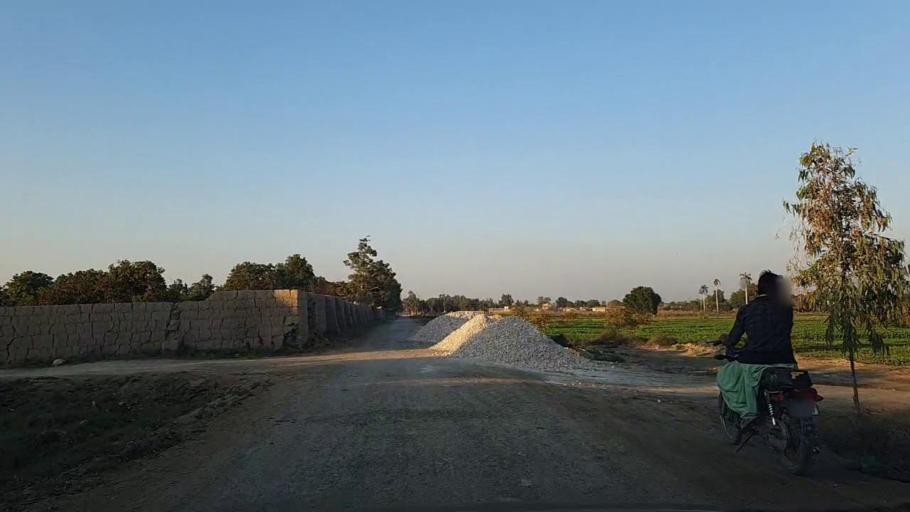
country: PK
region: Sindh
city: Nawabshah
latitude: 26.2435
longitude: 68.3383
